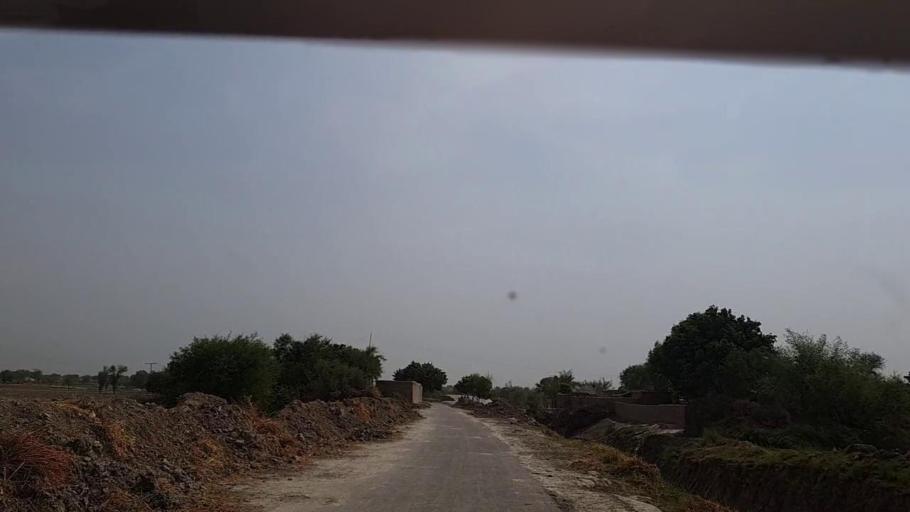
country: PK
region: Sindh
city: Khairpur Nathan Shah
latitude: 27.0539
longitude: 67.6840
